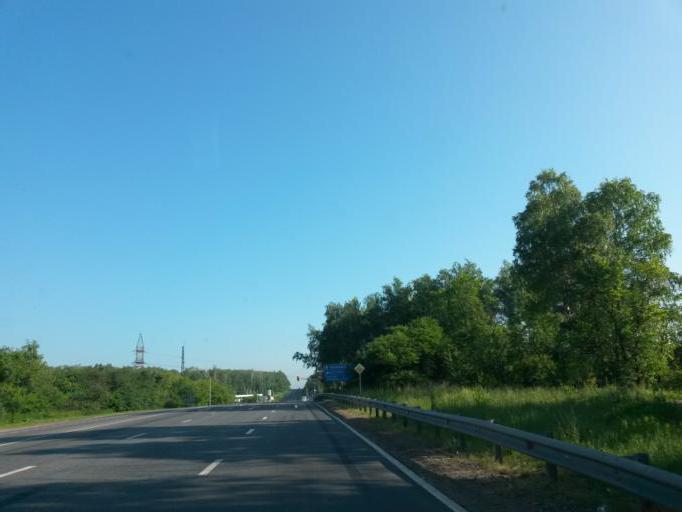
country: RU
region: Moskovskaya
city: Belyye Stolby
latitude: 55.3369
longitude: 37.8022
